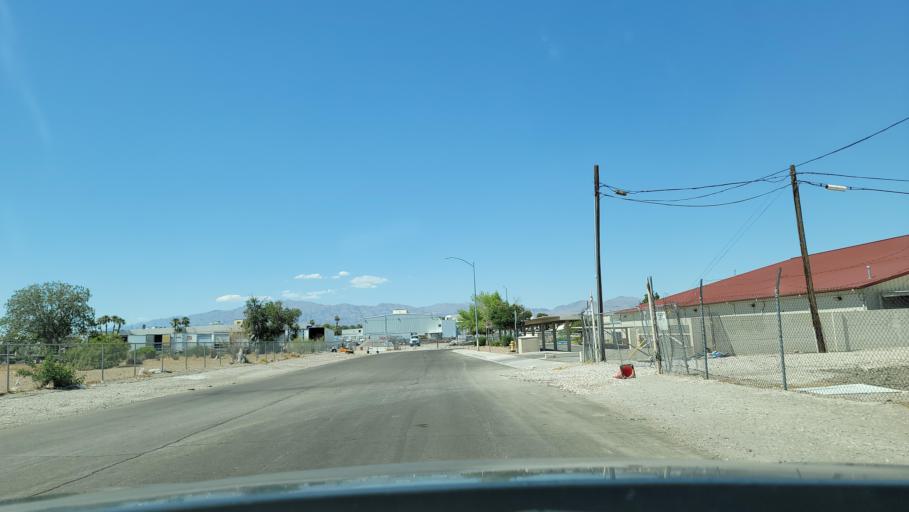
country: US
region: Nevada
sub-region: Clark County
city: Las Vegas
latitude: 36.1822
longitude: -115.1287
